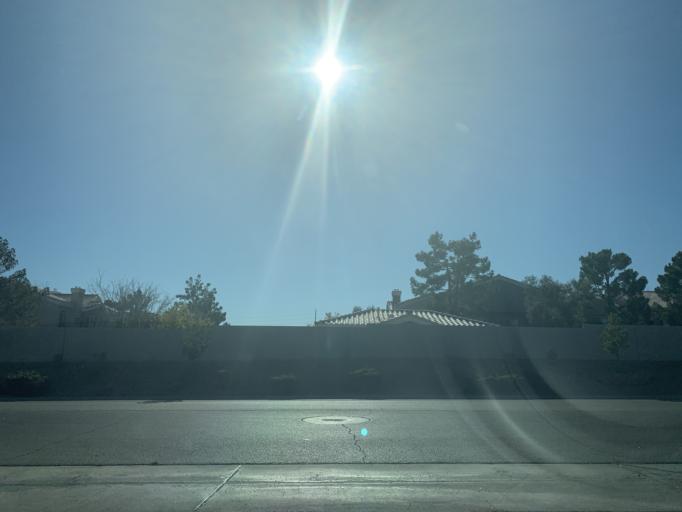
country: US
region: Nevada
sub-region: Clark County
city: Summerlin South
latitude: 36.1169
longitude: -115.2912
